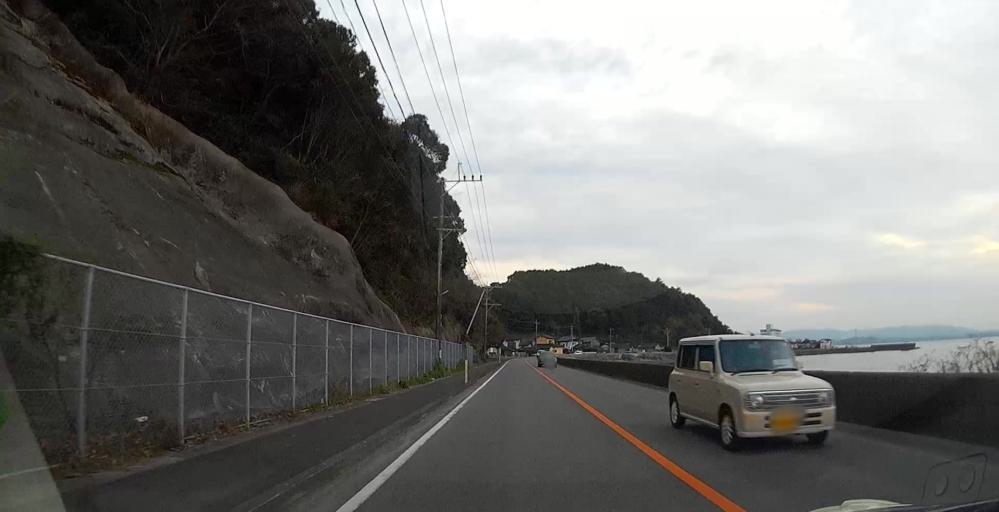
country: JP
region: Kumamoto
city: Hondo
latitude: 32.4847
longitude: 130.2832
